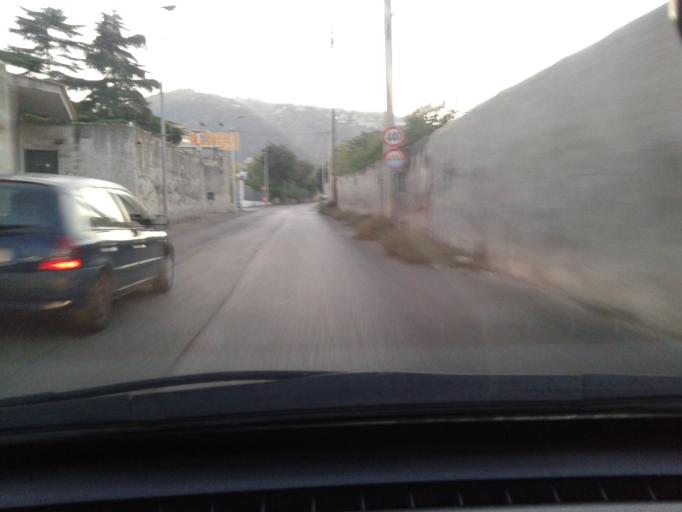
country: IT
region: Sicily
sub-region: Palermo
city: Palermo
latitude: 38.1044
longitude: 13.3251
